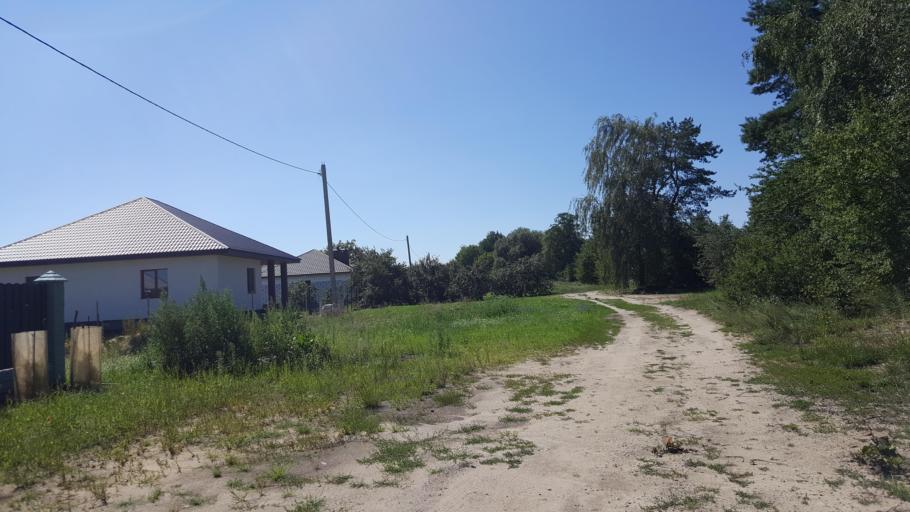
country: BY
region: Brest
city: Charnawchytsy
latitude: 52.2048
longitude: 23.7638
